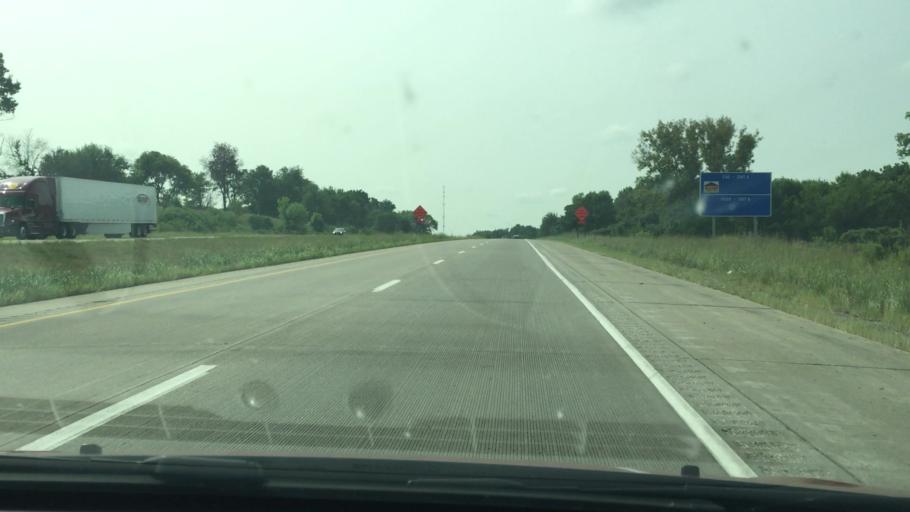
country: US
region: Iowa
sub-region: Scott County
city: Buffalo
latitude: 41.5204
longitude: -90.6745
